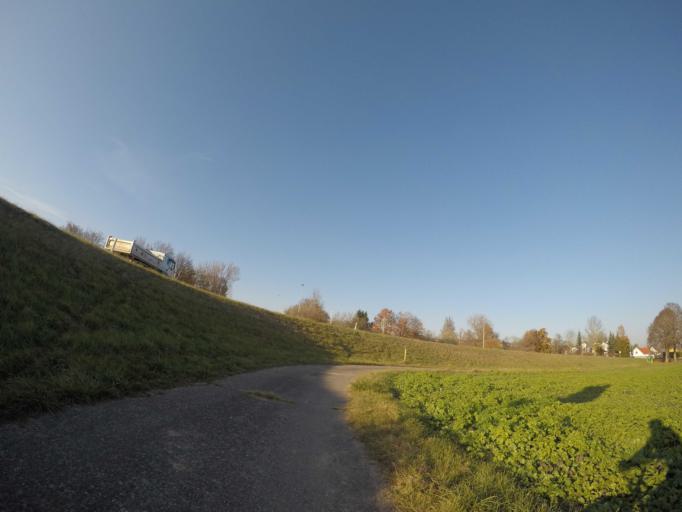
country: DE
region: Baden-Wuerttemberg
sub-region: Tuebingen Region
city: Rottenacker
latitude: 48.2301
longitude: 9.6905
